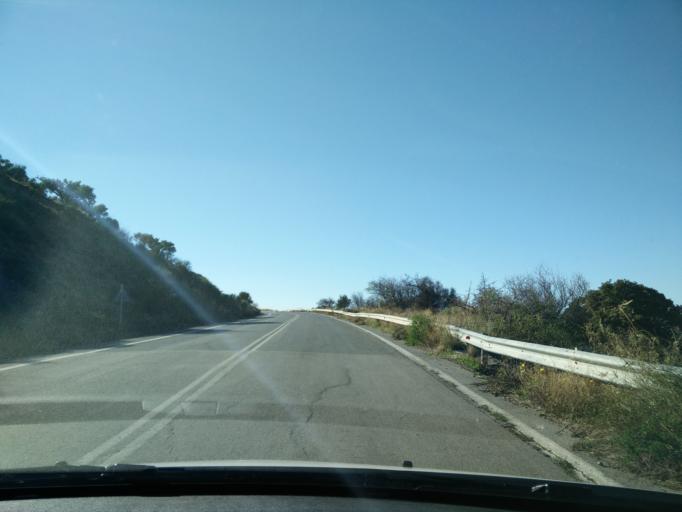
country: GR
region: Crete
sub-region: Nomos Irakleiou
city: Arkalochori
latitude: 35.0694
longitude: 25.3577
